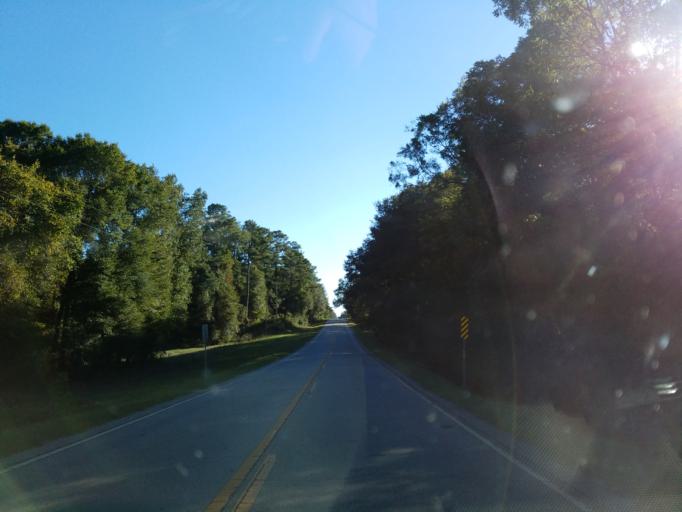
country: US
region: Georgia
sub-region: Lee County
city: Leesburg
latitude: 31.7663
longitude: -84.1461
